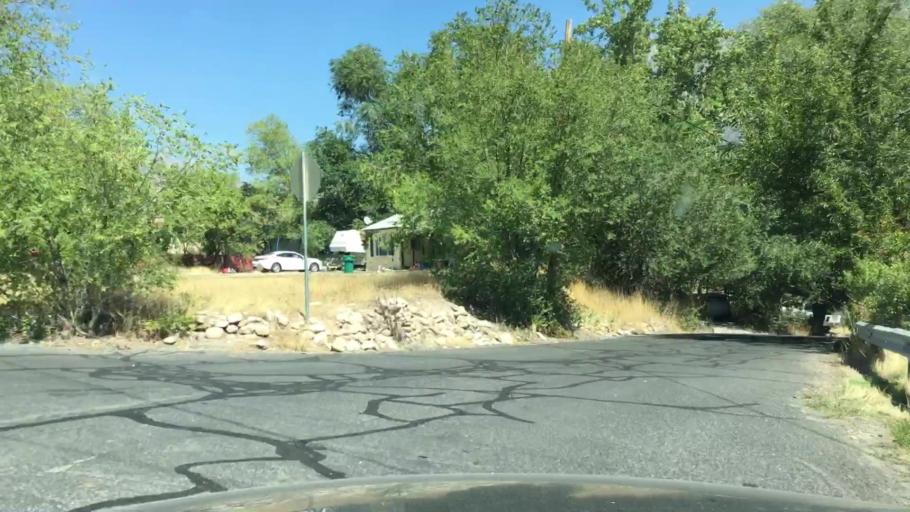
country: US
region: Utah
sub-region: Utah County
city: Provo
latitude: 40.2671
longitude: -111.6712
